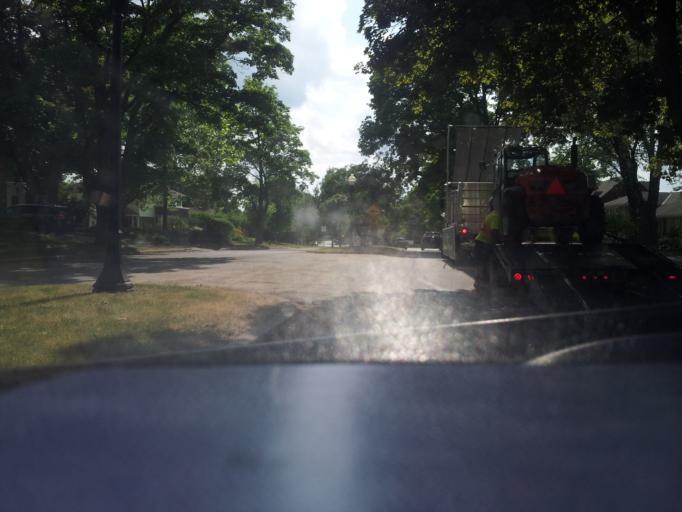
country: CA
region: Ontario
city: Waterloo
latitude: 43.4546
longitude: -80.5261
